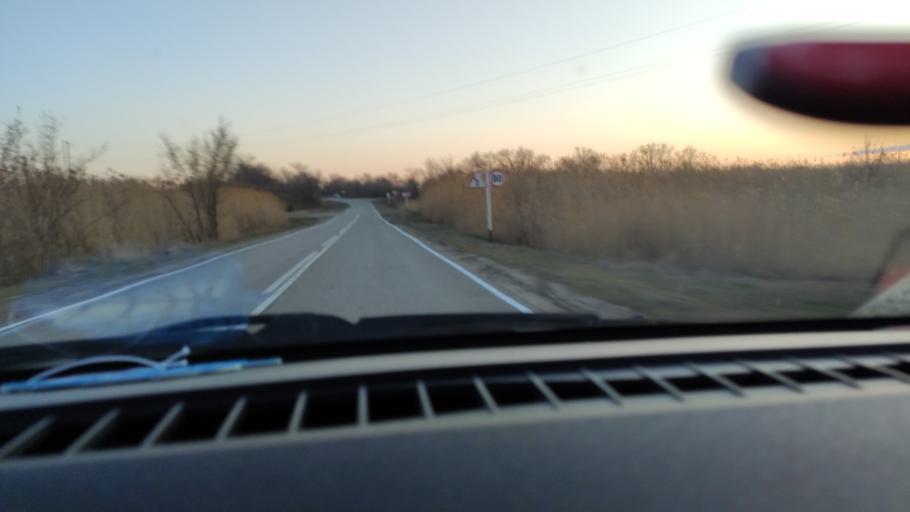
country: RU
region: Saratov
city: Privolzhskiy
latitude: 51.2328
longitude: 45.9218
